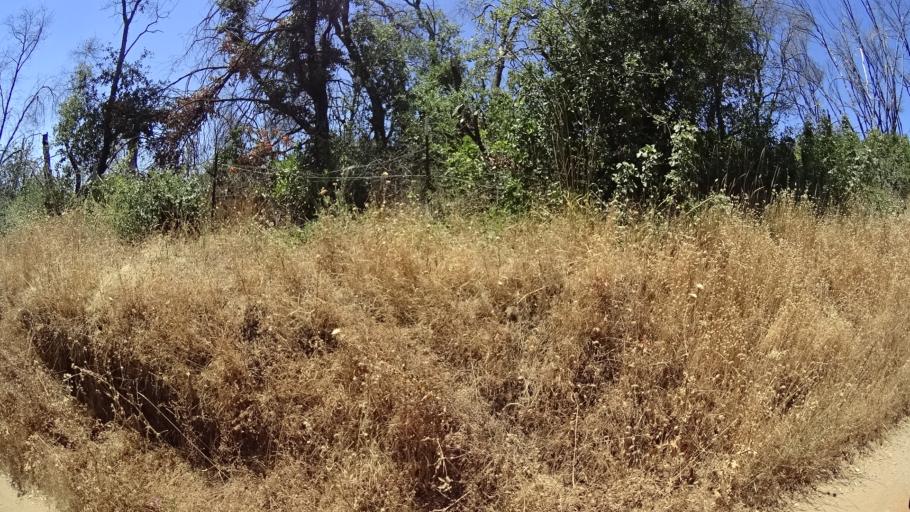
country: US
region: California
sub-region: Calaveras County
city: Mountain Ranch
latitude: 38.2847
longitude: -120.5982
